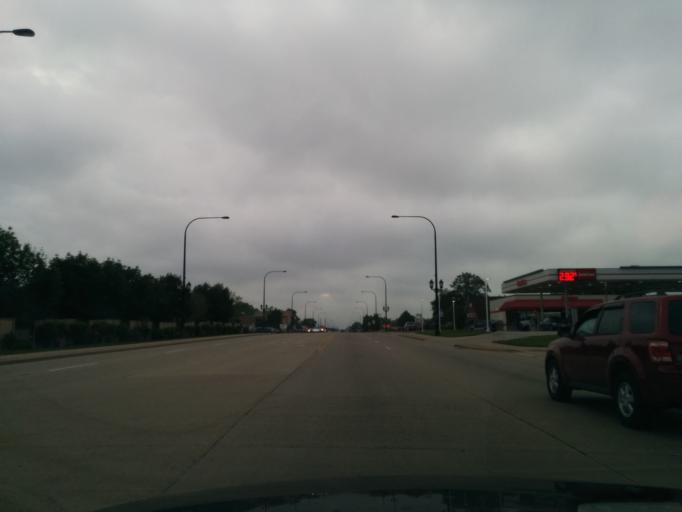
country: US
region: Illinois
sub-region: DuPage County
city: Addison
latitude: 41.9408
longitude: -88.0087
